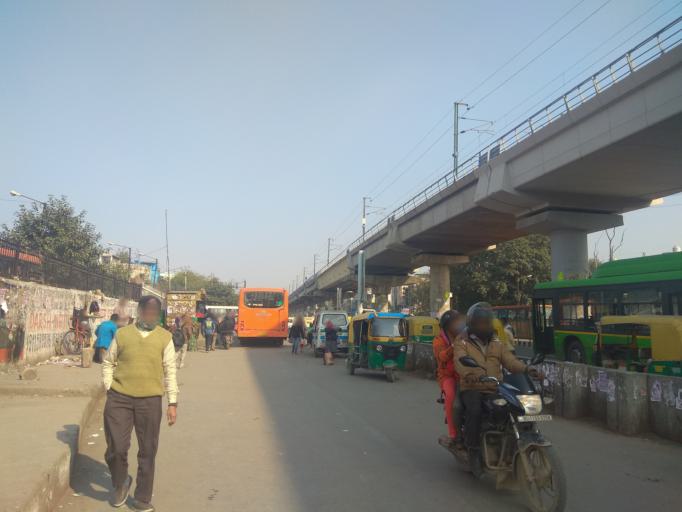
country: IN
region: NCT
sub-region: West Delhi
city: Nangloi Jat
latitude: 28.6252
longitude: 77.0659
